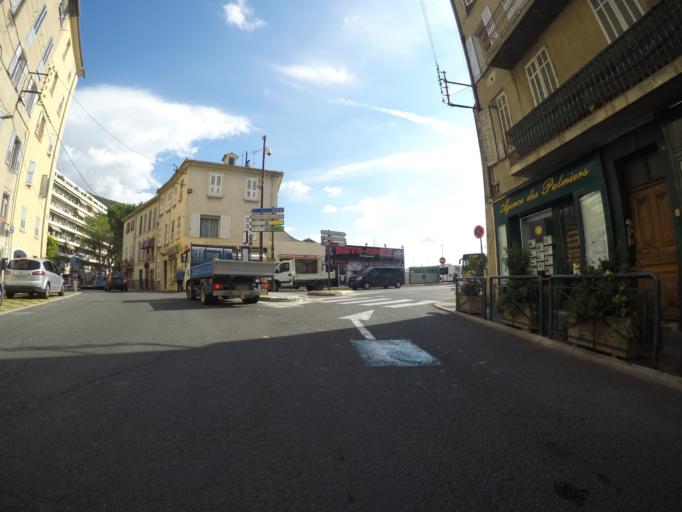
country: FR
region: Provence-Alpes-Cote d'Azur
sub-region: Departement des Alpes-Maritimes
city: Grasse
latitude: 43.6609
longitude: 6.9228
